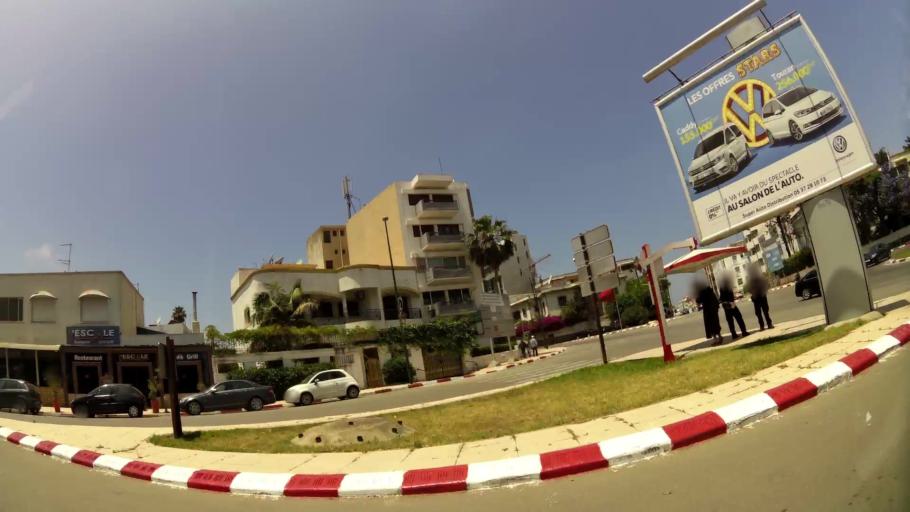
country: MA
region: Rabat-Sale-Zemmour-Zaer
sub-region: Rabat
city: Rabat
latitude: 34.0170
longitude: -6.8237
